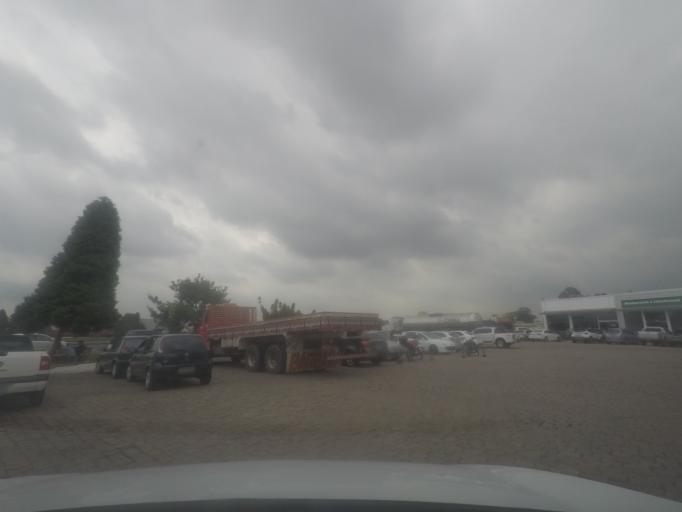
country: BR
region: Parana
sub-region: Sao Jose Dos Pinhais
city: Sao Jose dos Pinhais
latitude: -25.5420
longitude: -49.3090
